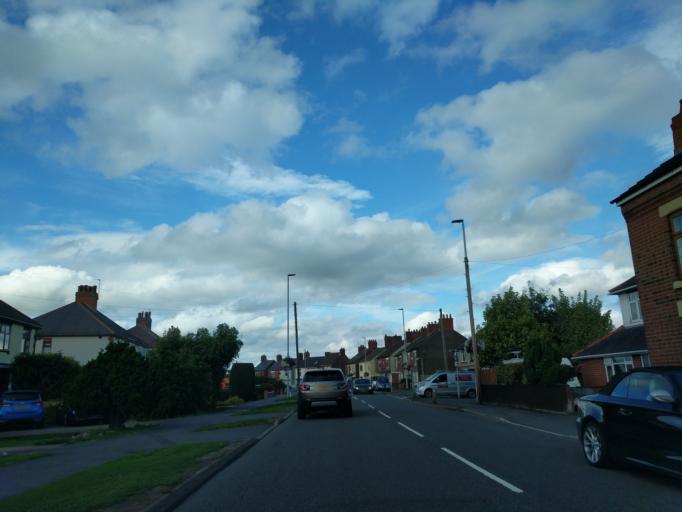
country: GB
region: England
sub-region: Leicestershire
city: Ibstock
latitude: 52.6939
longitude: -1.4022
